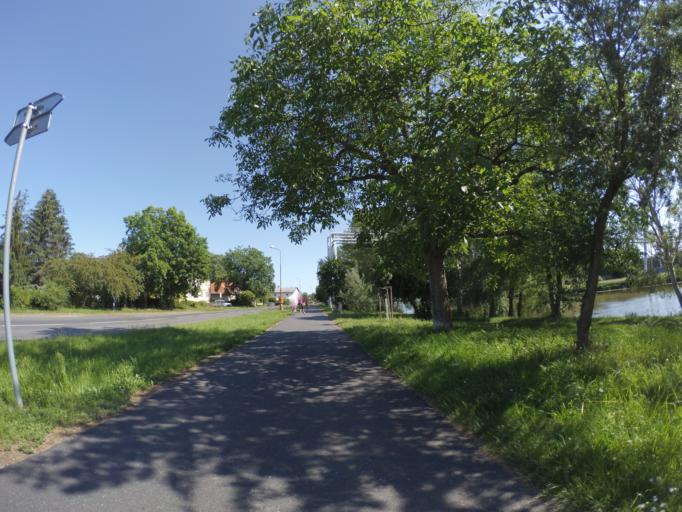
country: CZ
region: Central Bohemia
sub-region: Okres Nymburk
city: Podebrady
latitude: 50.1585
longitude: 15.1050
